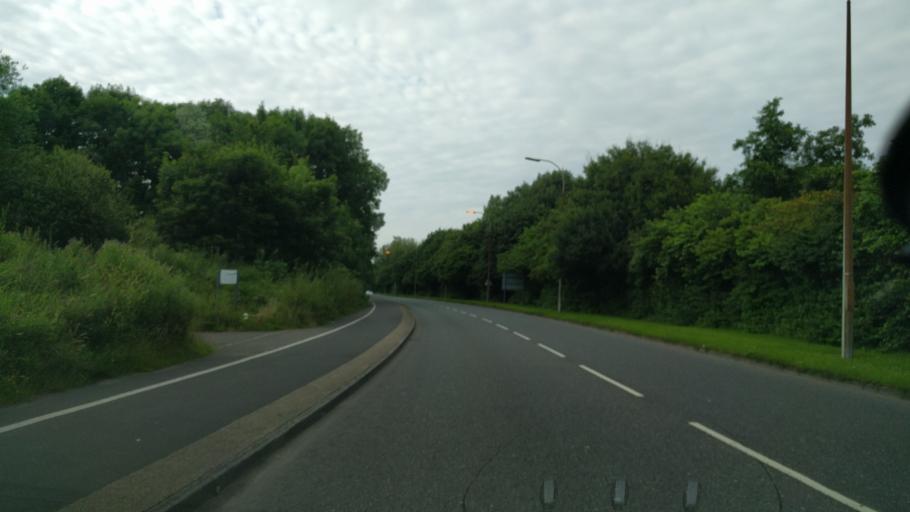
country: GB
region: England
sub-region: Warrington
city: Warrington
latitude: 53.4082
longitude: -2.5606
